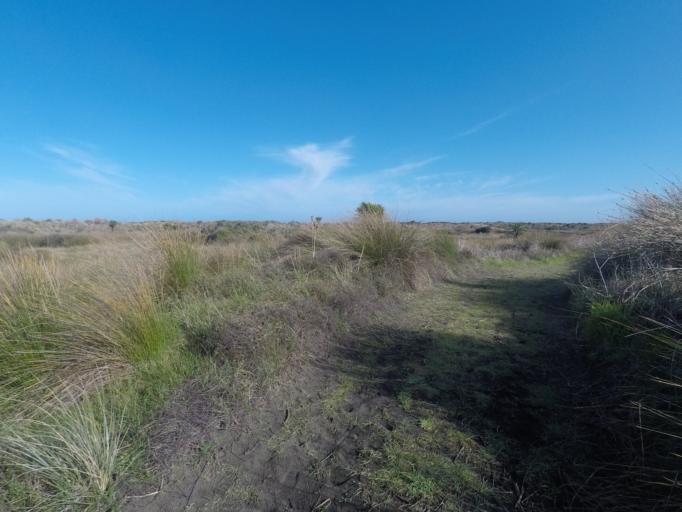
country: NZ
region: Auckland
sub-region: Auckland
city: Titirangi
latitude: -37.0083
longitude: 174.4804
